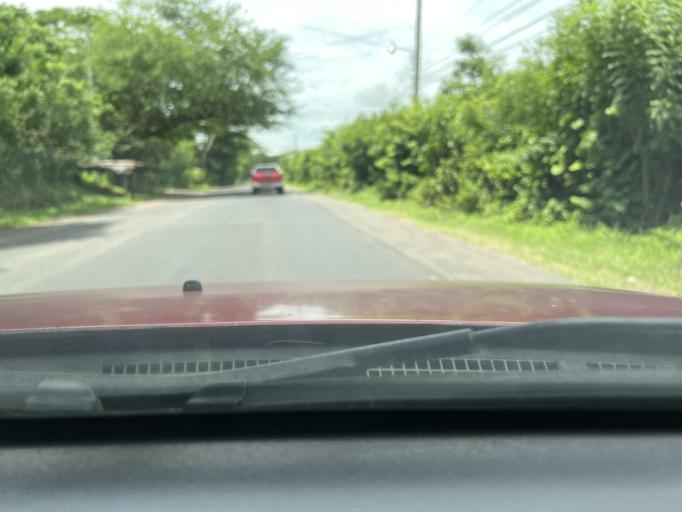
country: SV
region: Usulutan
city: Berlin
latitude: 13.6025
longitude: -88.5875
